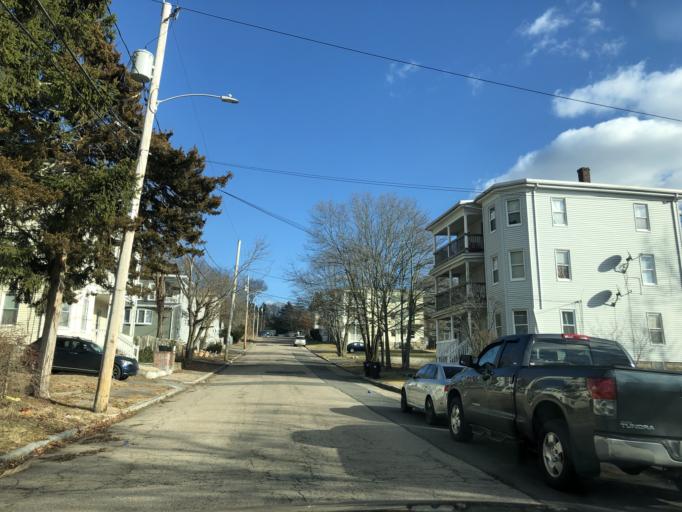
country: US
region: Massachusetts
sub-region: Plymouth County
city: Brockton
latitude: 42.1048
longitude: -71.0127
